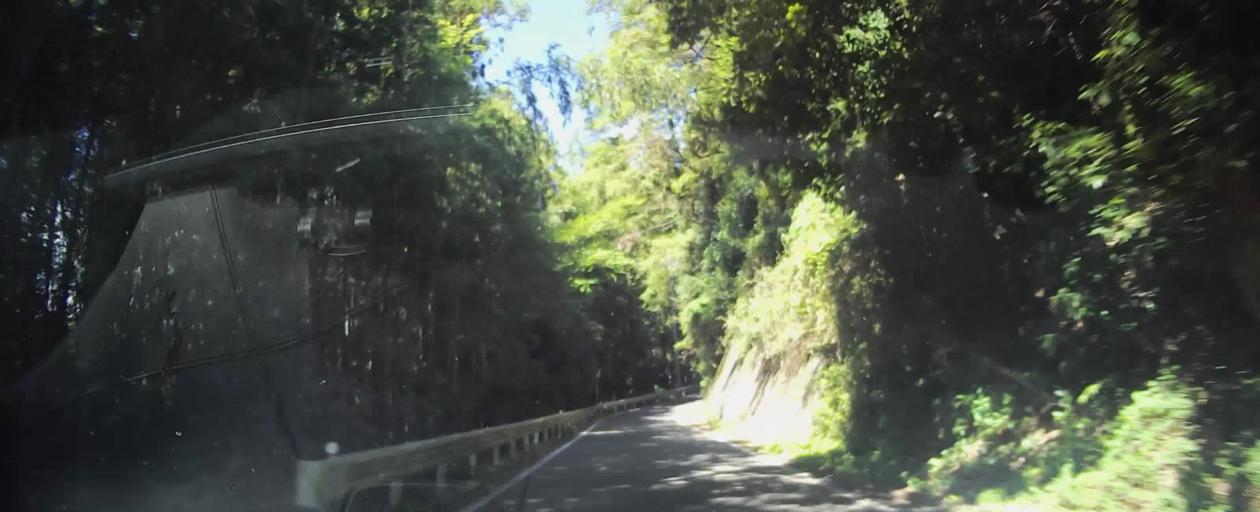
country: JP
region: Gunma
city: Kanekomachi
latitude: 36.4035
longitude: 138.9496
